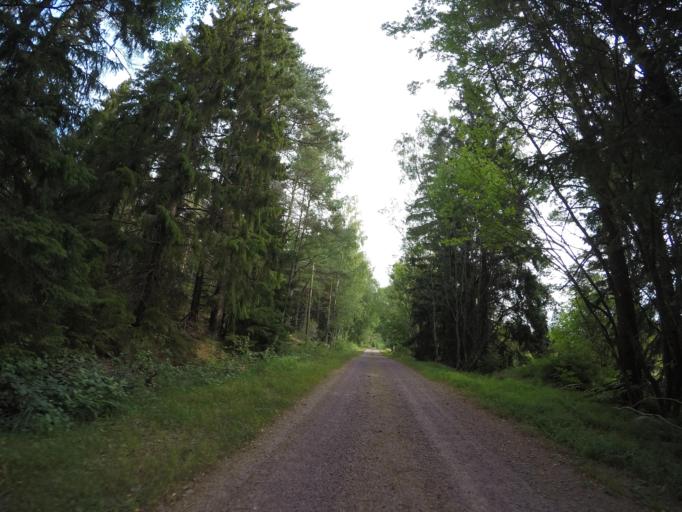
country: AX
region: Alands landsbygd
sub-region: Hammarland
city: Hammarland
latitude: 60.2253
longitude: 19.8458
